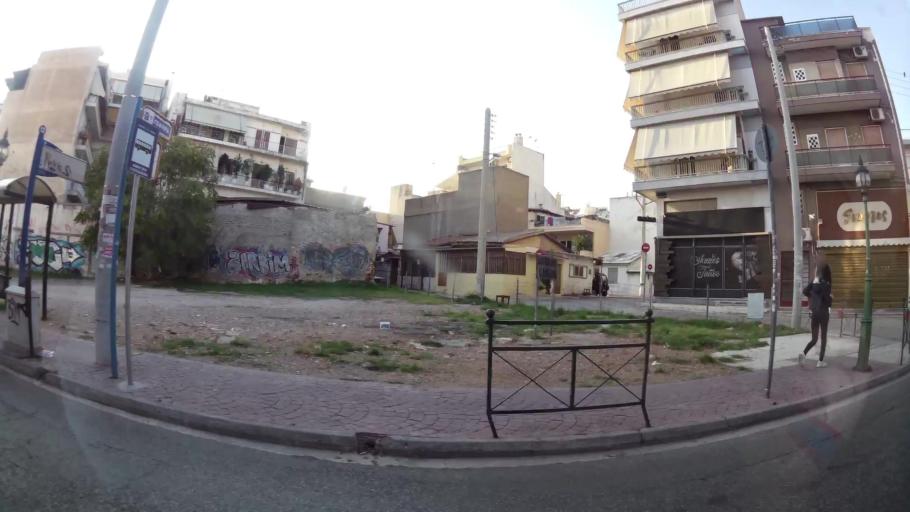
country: GR
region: Attica
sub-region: Nomos Piraios
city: Nikaia
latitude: 37.9645
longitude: 23.6495
